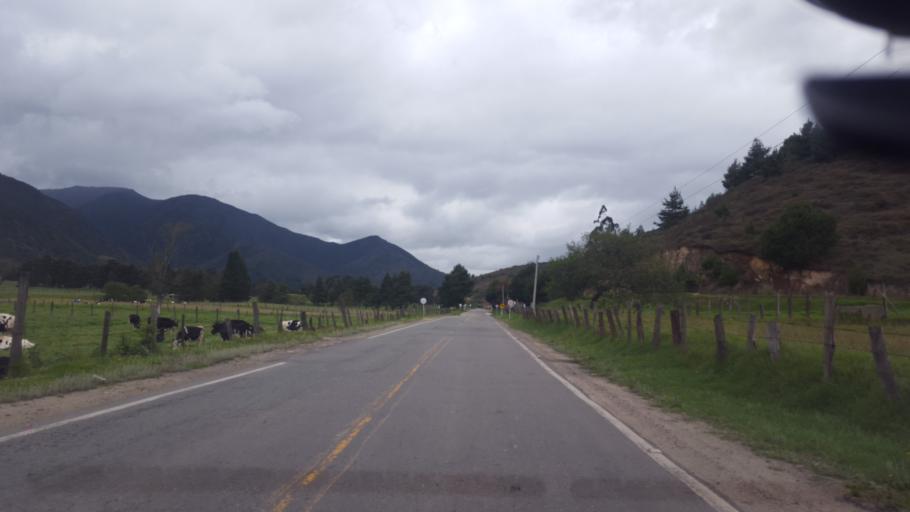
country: CO
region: Boyaca
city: Belen
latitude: 5.9996
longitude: -72.8474
